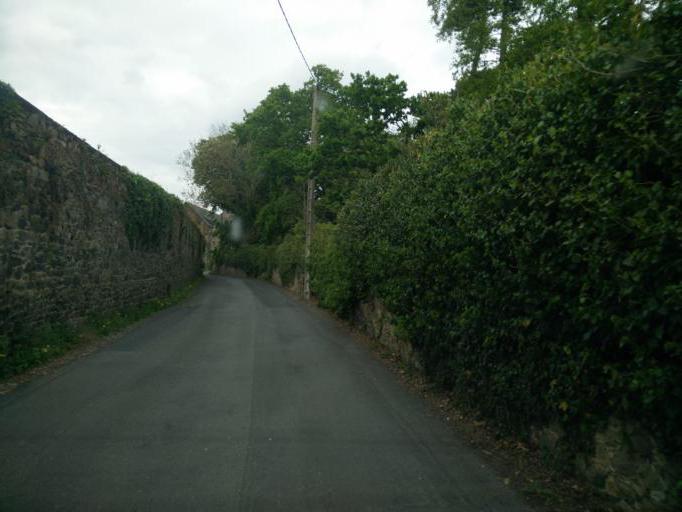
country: FR
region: Brittany
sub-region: Departement des Cotes-d'Armor
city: Langueux
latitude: 48.5074
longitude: -2.7026
